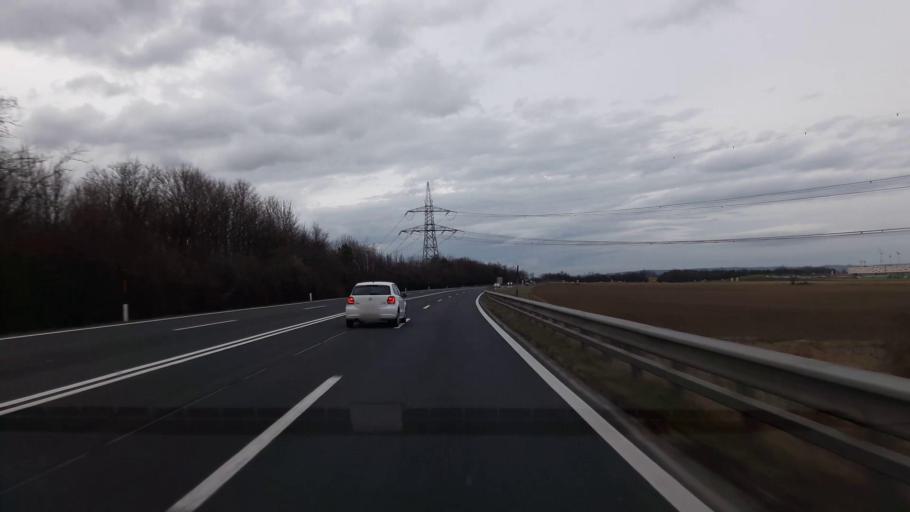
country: AT
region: Burgenland
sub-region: Politischer Bezirk Mattersburg
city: Mattersburg
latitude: 47.7357
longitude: 16.3721
